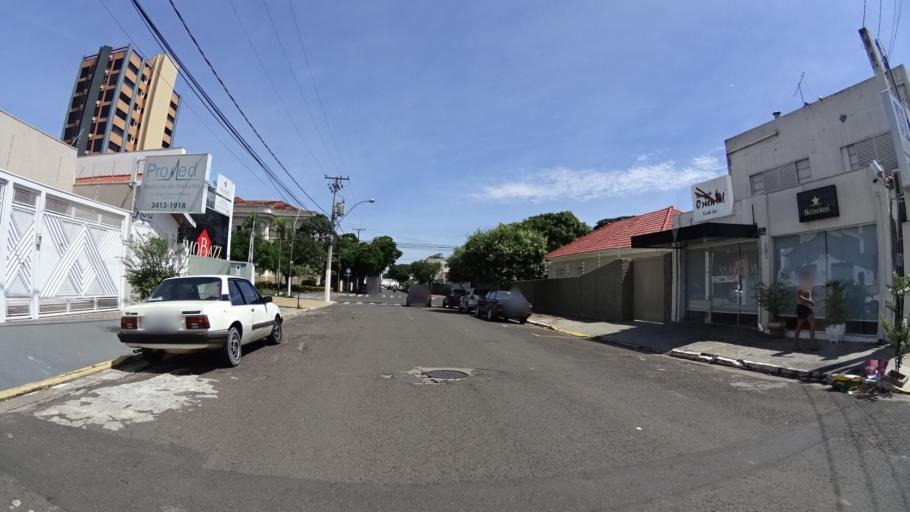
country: BR
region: Sao Paulo
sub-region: Marilia
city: Marilia
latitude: -22.2197
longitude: -49.9459
